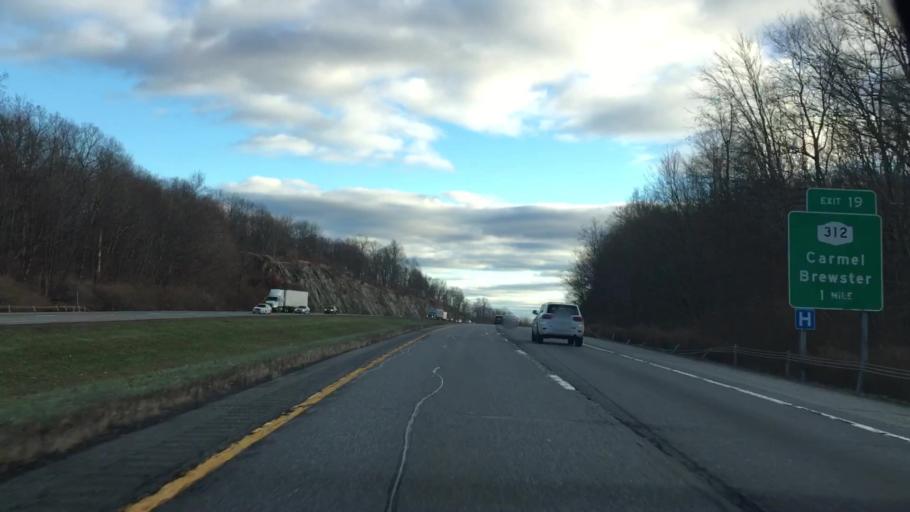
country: US
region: New York
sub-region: Putnam County
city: Brewster Hill
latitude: 41.4423
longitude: -73.6333
